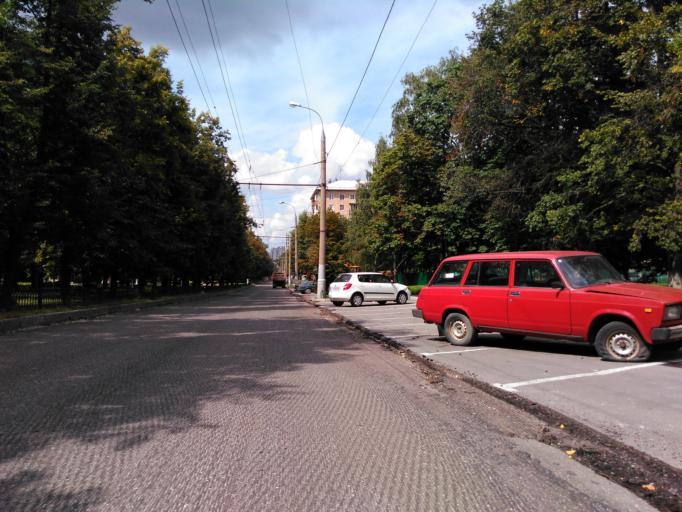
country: RU
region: Moskovskaya
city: Semenovskoye
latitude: 55.6789
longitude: 37.5287
